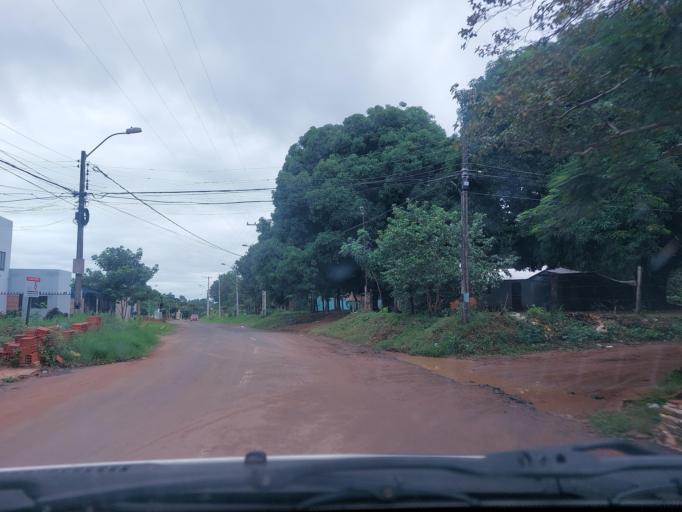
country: PY
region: San Pedro
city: Guayaybi
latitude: -24.6788
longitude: -56.4500
